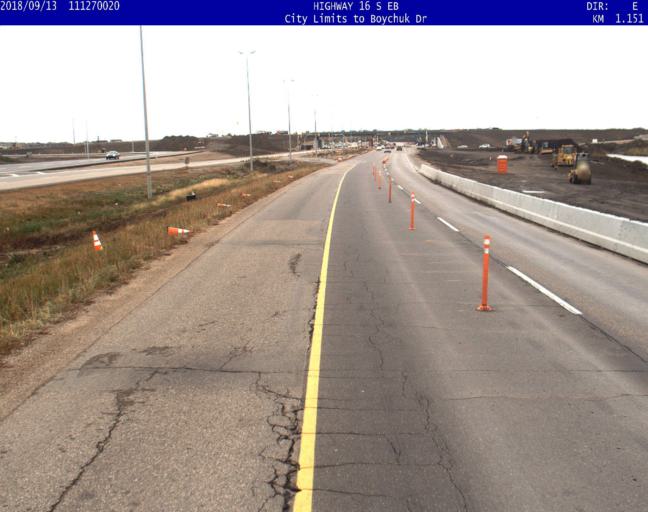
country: CA
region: Saskatchewan
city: Saskatoon
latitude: 52.0887
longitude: -106.5811
